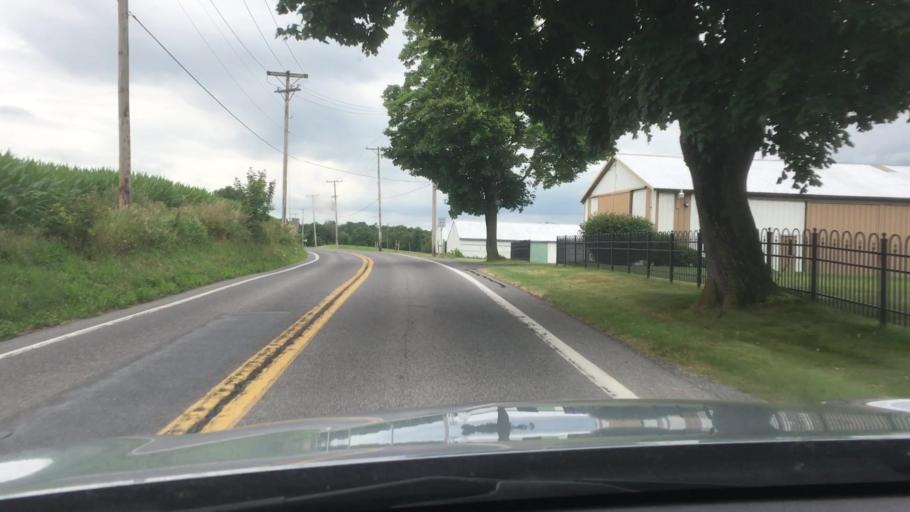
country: US
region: Pennsylvania
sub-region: Franklin County
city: Chambersburg
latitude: 39.8859
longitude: -77.7249
